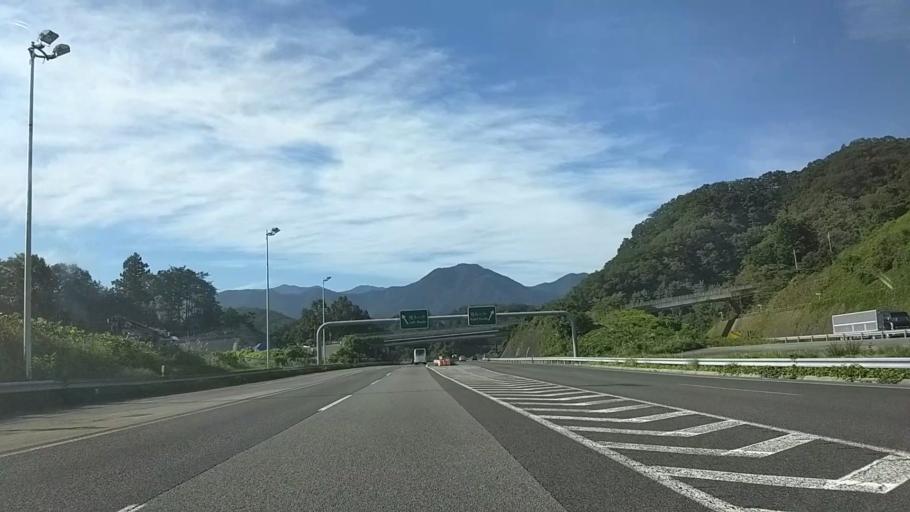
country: JP
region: Yamanashi
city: Uenohara
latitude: 35.6256
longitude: 139.0433
